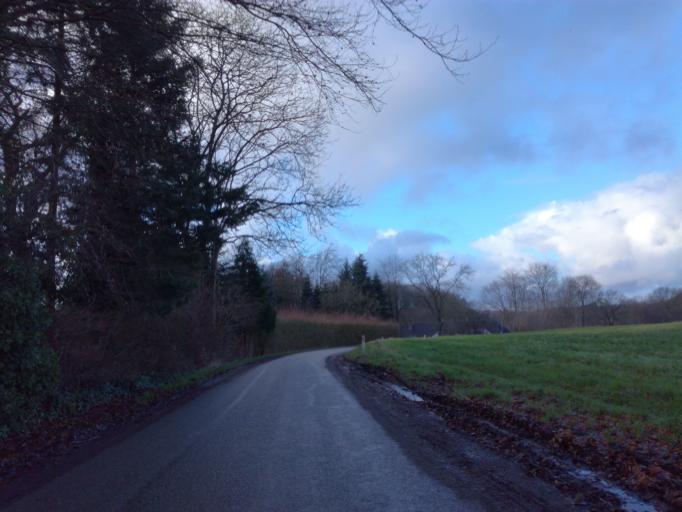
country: DK
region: South Denmark
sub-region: Fredericia Kommune
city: Taulov
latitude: 55.5616
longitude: 9.6369
